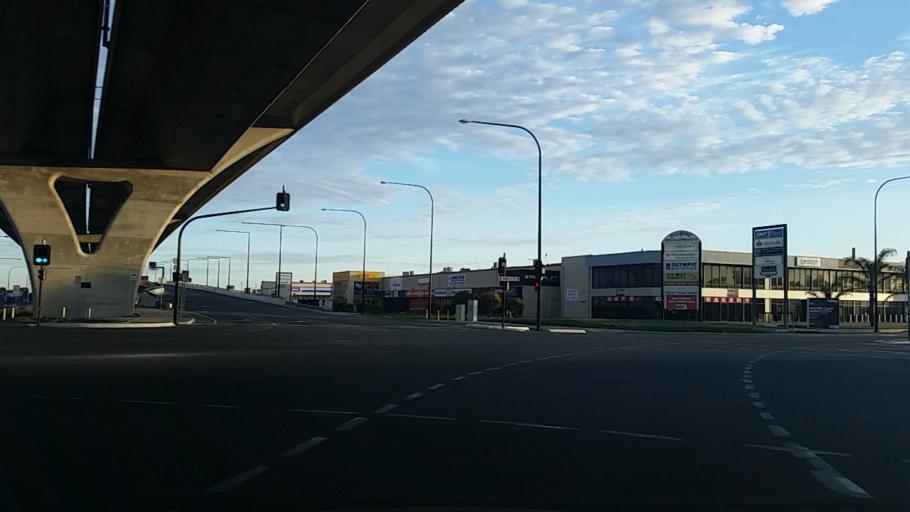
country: AU
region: South Australia
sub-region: Charles Sturt
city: Woodville North
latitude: -34.8499
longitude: 138.5646
